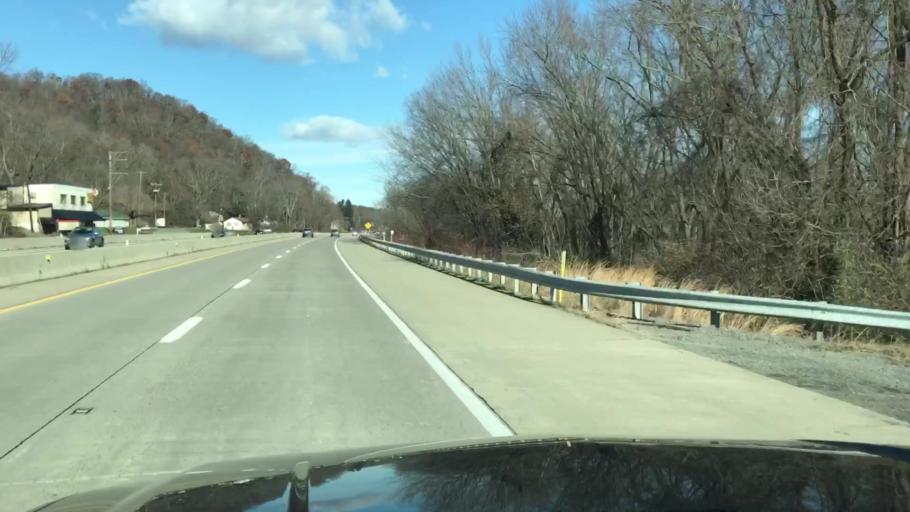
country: US
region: Pennsylvania
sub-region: Dauphin County
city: Millersburg
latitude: 40.6132
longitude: -76.9540
